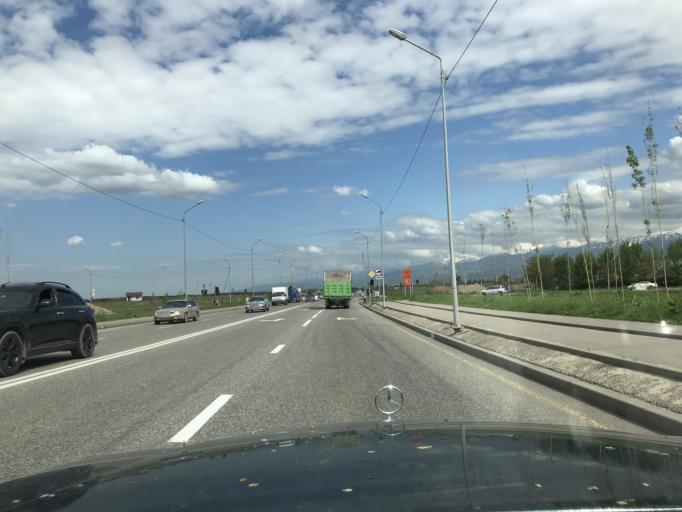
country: KZ
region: Almaty Oblysy
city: Burunday
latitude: 43.3136
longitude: 76.8409
